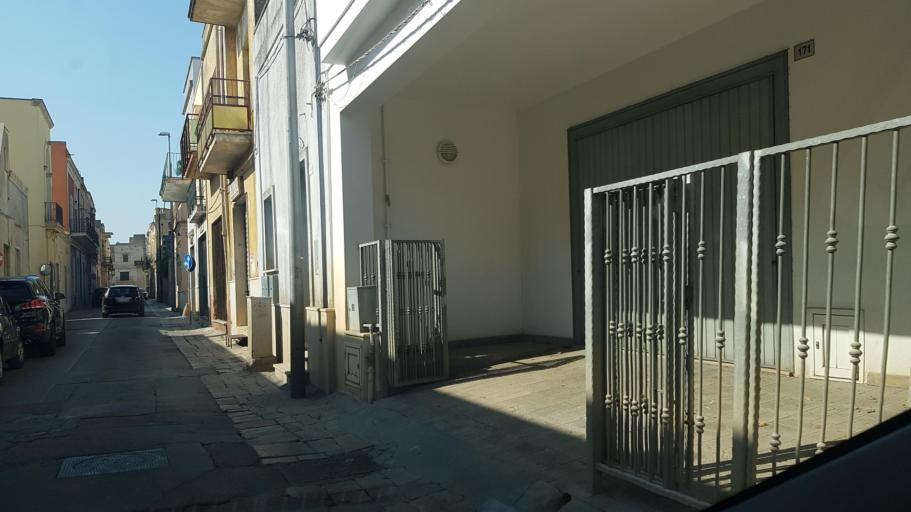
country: IT
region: Apulia
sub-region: Provincia di Lecce
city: Taurisano
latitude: 39.9541
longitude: 18.2151
